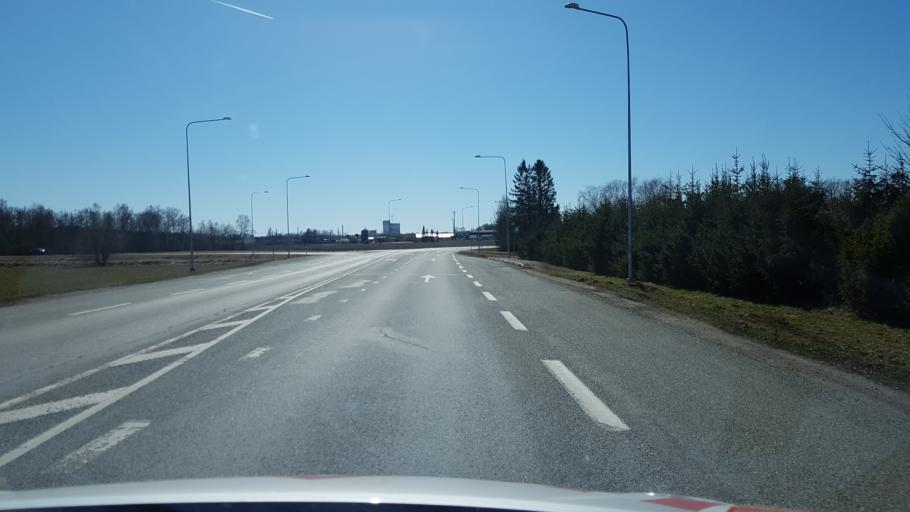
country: EE
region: Laeaene-Virumaa
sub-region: Rakvere linn
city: Rakvere
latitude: 59.3738
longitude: 26.3867
